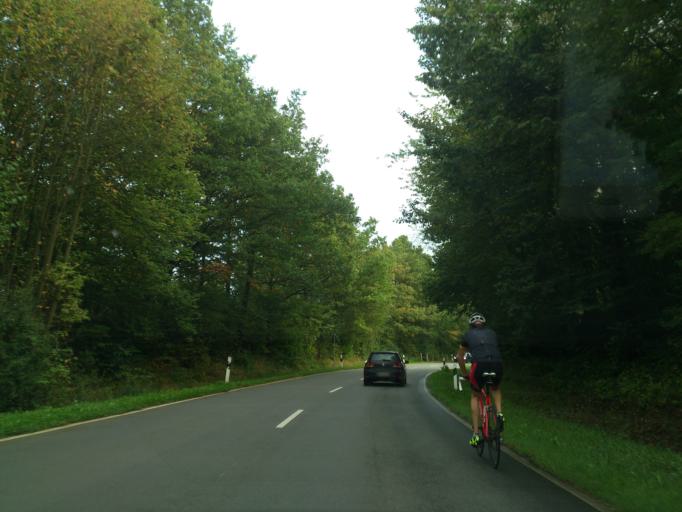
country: DE
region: North Rhine-Westphalia
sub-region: Regierungsbezirk Detmold
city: Altenbeken
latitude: 51.7096
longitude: 8.9436
